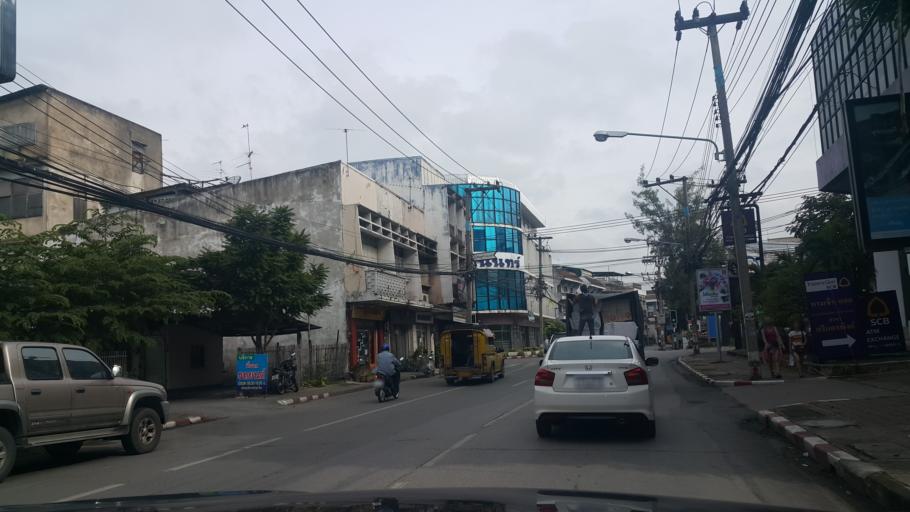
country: TH
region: Chiang Mai
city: Chiang Mai
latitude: 18.7917
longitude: 98.9979
